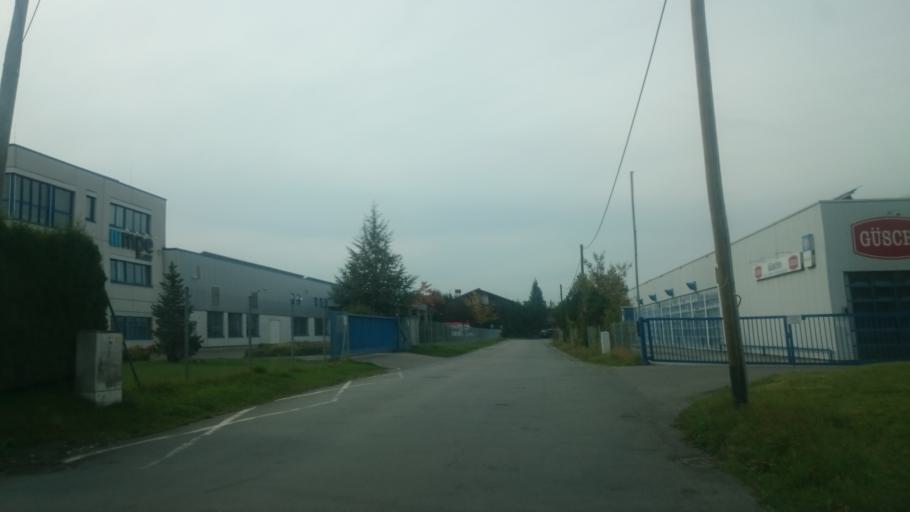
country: DE
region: Bavaria
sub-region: Swabia
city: Fuessen
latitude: 47.5755
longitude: 10.6758
